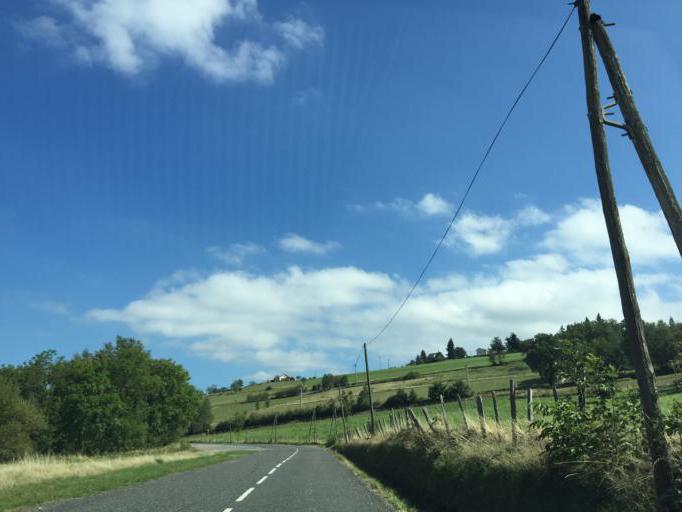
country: FR
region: Rhone-Alpes
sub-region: Departement de la Loire
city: Saint-Paul-en-Jarez
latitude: 45.4411
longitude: 4.5775
